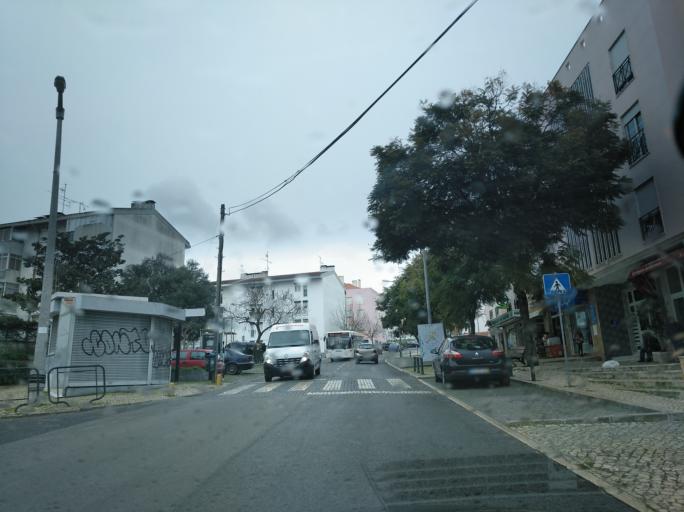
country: PT
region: Lisbon
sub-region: Odivelas
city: Famoes
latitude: 38.7914
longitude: -9.2104
